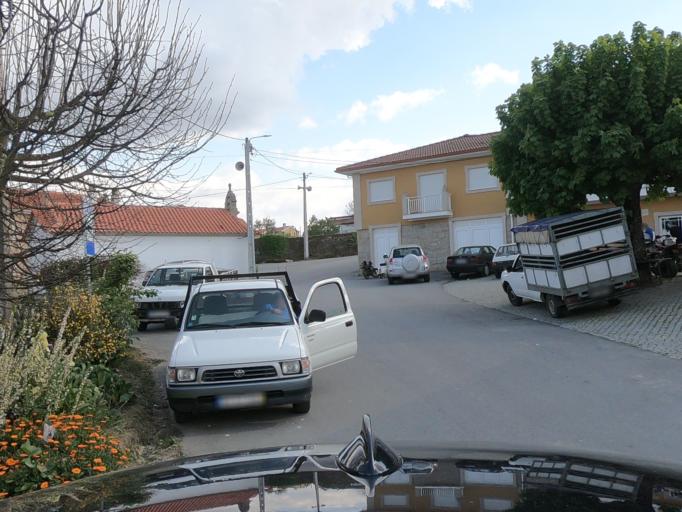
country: PT
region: Vila Real
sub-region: Sabrosa
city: Vilela
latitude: 41.2408
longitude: -7.6561
